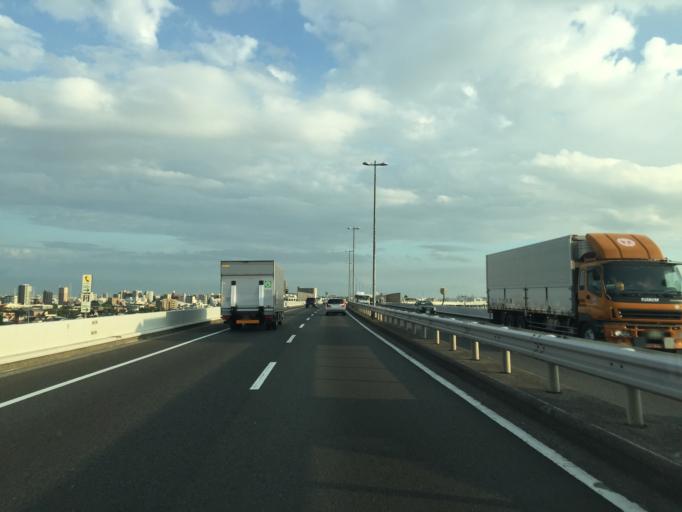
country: JP
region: Tokyo
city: Urayasu
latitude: 35.7002
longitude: 139.8597
